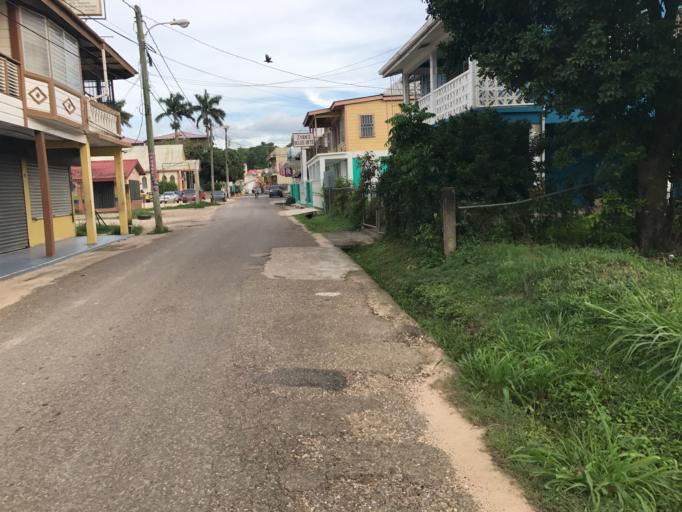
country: BZ
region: Cayo
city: San Ignacio
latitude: 17.1602
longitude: -89.0708
